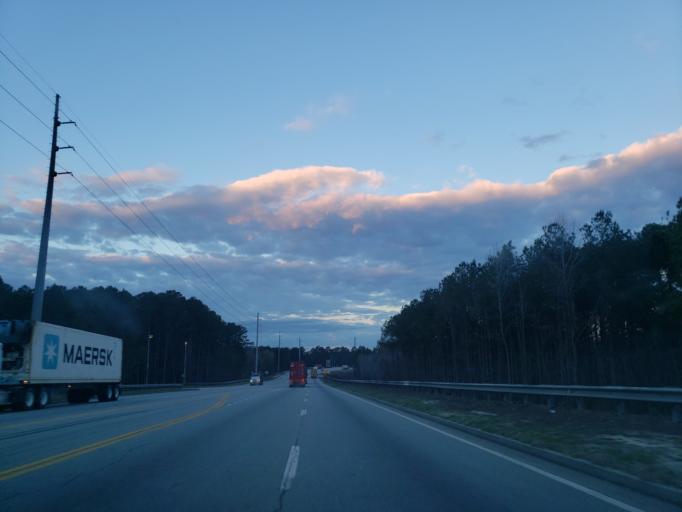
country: US
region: Georgia
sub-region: Chatham County
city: Port Wentworth
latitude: 32.1637
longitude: -81.2046
